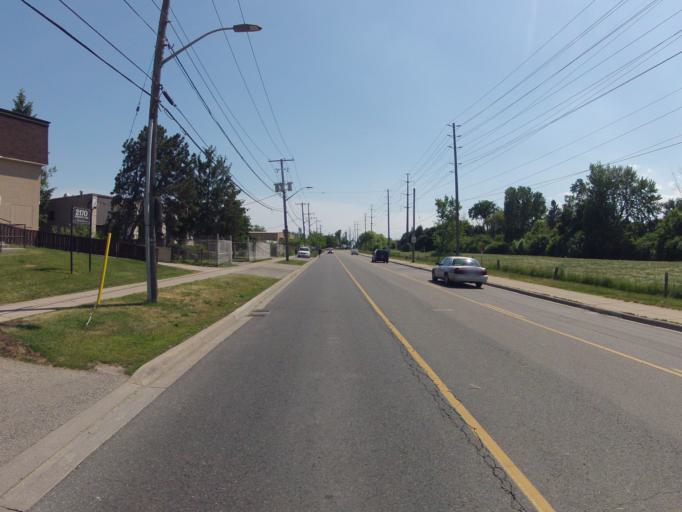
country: CA
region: Ontario
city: Mississauga
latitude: 43.5115
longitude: -79.6382
